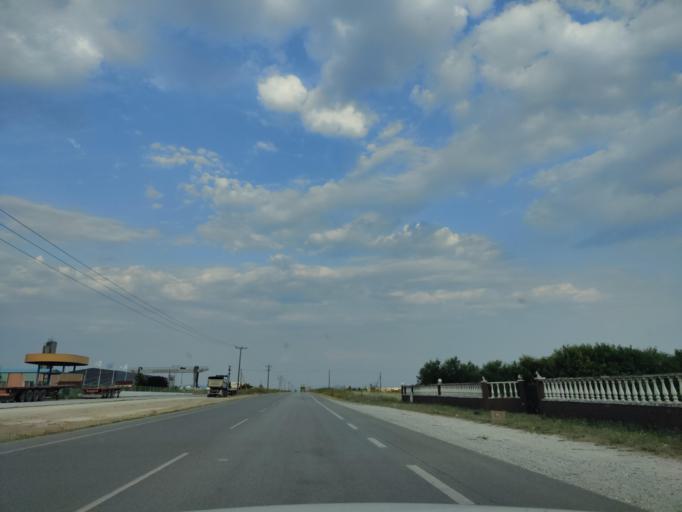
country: GR
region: East Macedonia and Thrace
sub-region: Nomos Dramas
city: Prosotsani
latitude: 41.1789
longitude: 23.9939
